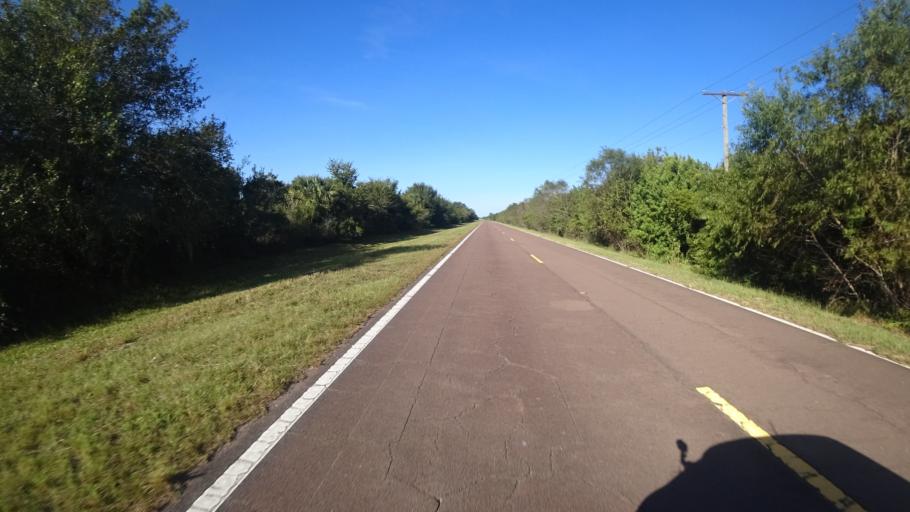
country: US
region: Florida
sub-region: Hillsborough County
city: Ruskin
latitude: 27.6540
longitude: -82.4657
